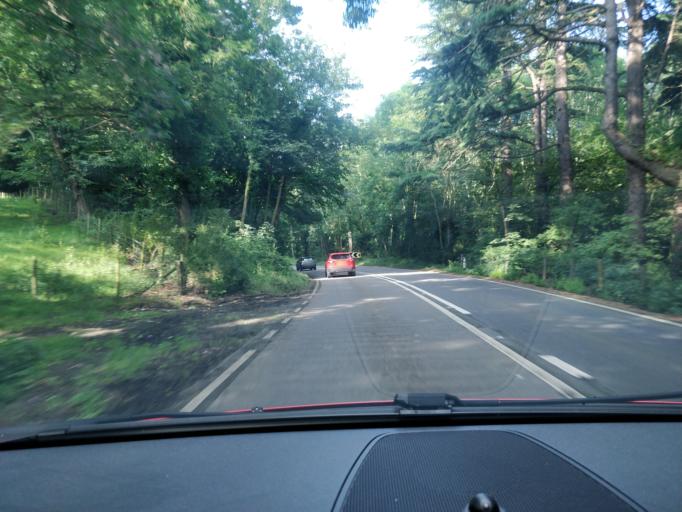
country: GB
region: Wales
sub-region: Conwy
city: Llansantffraid Glan Conwy
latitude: 53.2399
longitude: -3.8029
